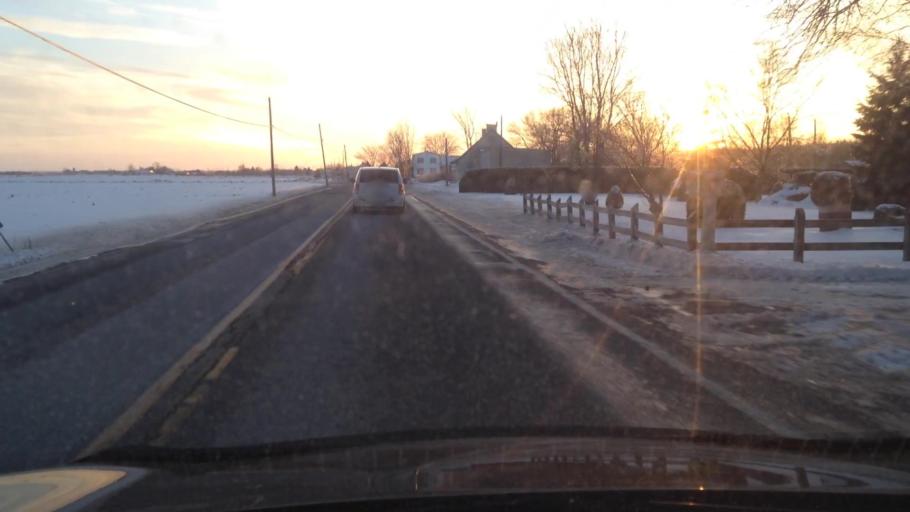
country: CA
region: Quebec
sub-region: Lanaudiere
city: Saint-Lin-Laurentides
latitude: 45.9043
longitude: -73.7479
